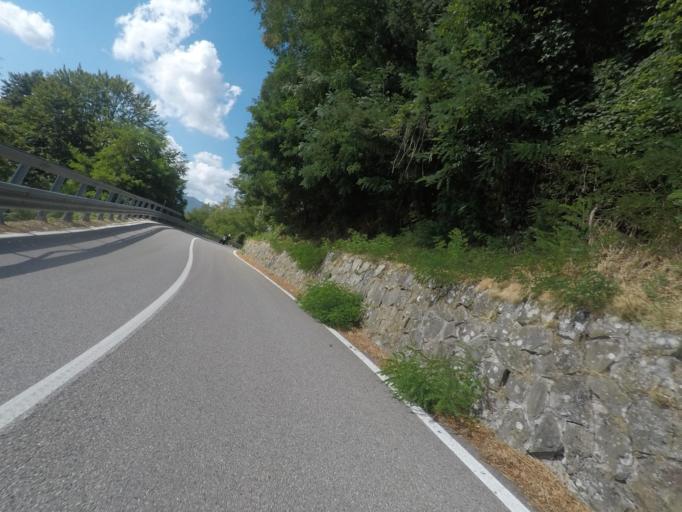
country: IT
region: Tuscany
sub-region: Provincia di Massa-Carrara
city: Comano
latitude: 44.2689
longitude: 10.1790
